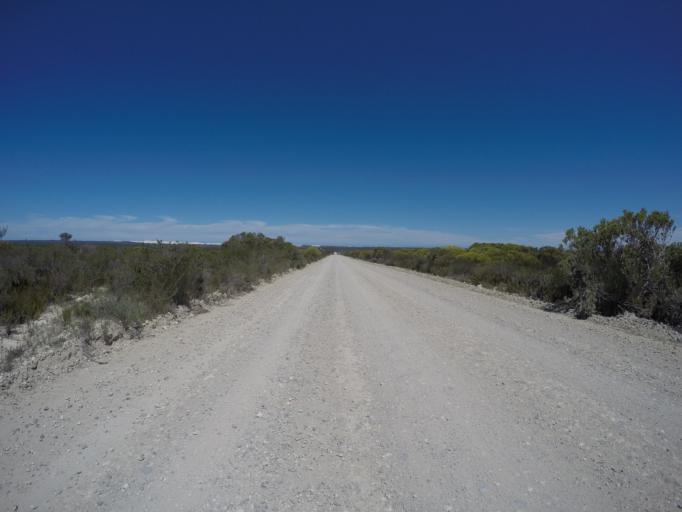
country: ZA
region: Western Cape
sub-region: Overberg District Municipality
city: Bredasdorp
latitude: -34.4371
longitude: 20.4204
